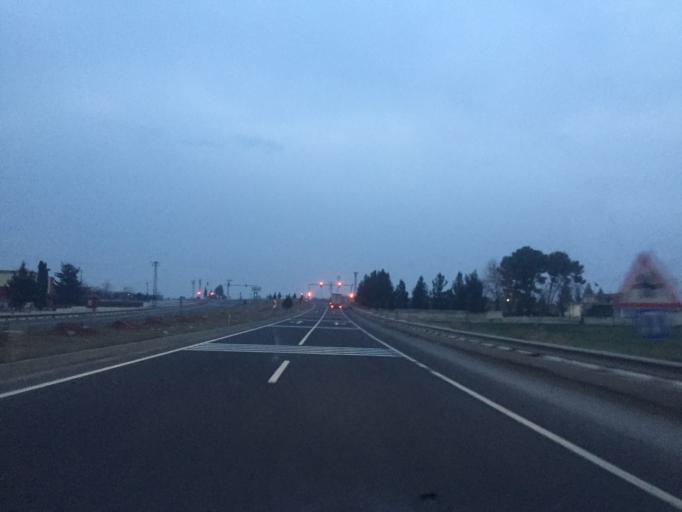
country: TR
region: Sanliurfa
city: Camlidere
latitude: 37.1537
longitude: 39.0668
